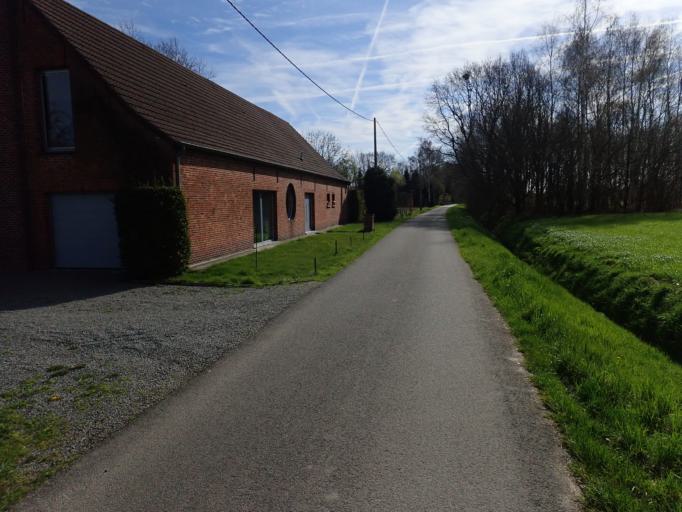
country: BE
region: Flanders
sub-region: Provincie Antwerpen
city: Lier
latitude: 51.1566
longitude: 4.5440
